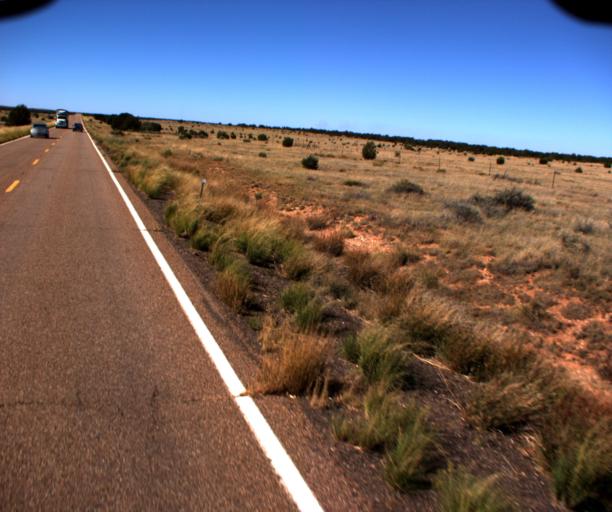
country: US
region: Arizona
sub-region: Navajo County
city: Heber-Overgaard
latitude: 34.4762
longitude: -110.3492
